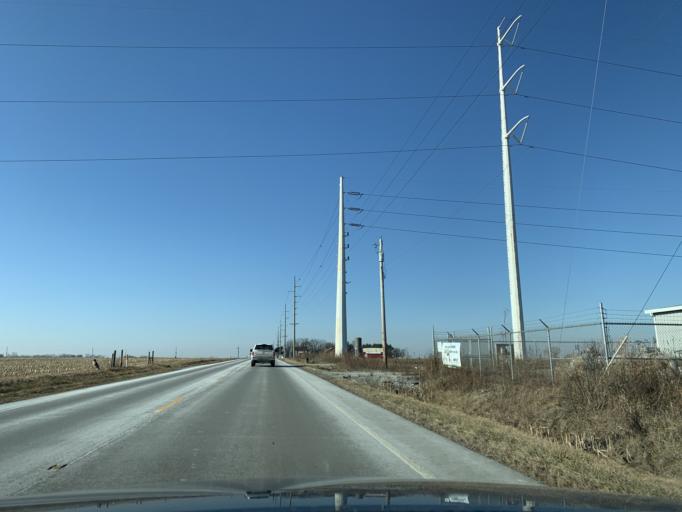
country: US
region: Indiana
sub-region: Lake County
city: Saint John
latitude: 41.4209
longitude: -87.4240
